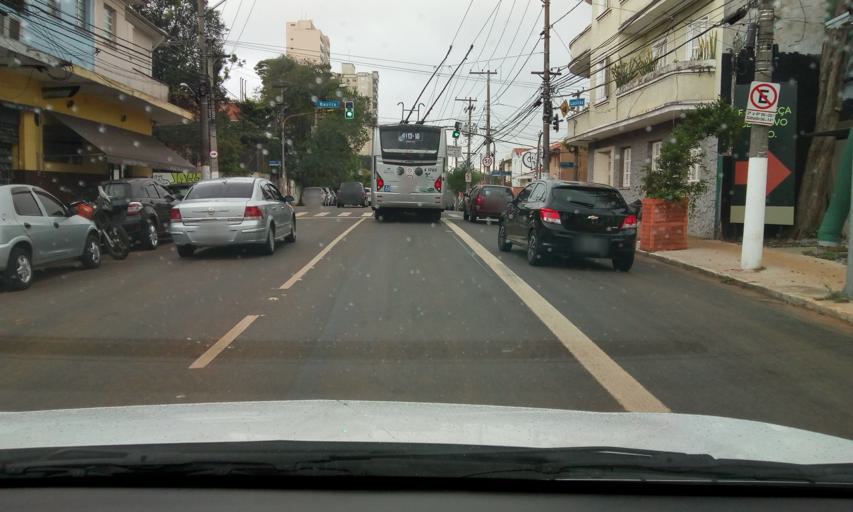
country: BR
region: Sao Paulo
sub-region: Sao Paulo
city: Sao Paulo
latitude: -23.5766
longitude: -46.6251
